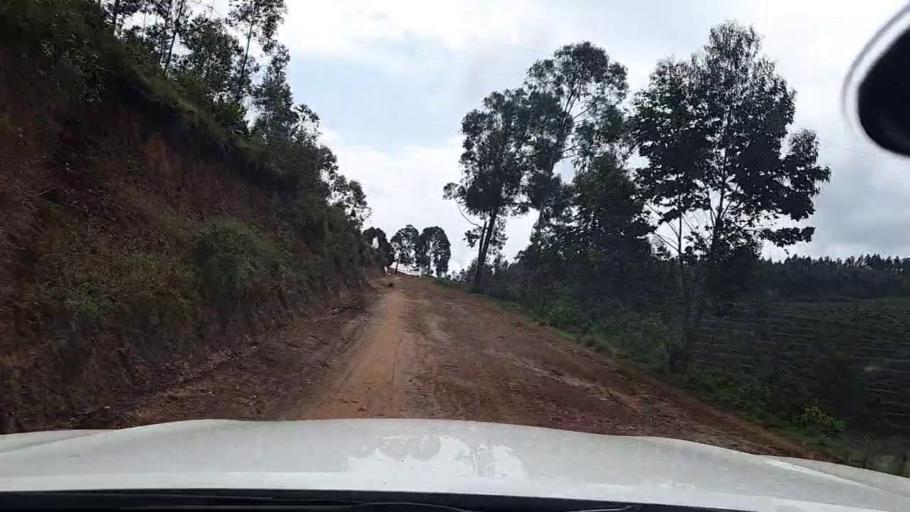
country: RW
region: Western Province
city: Kibuye
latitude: -2.1304
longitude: 29.3748
